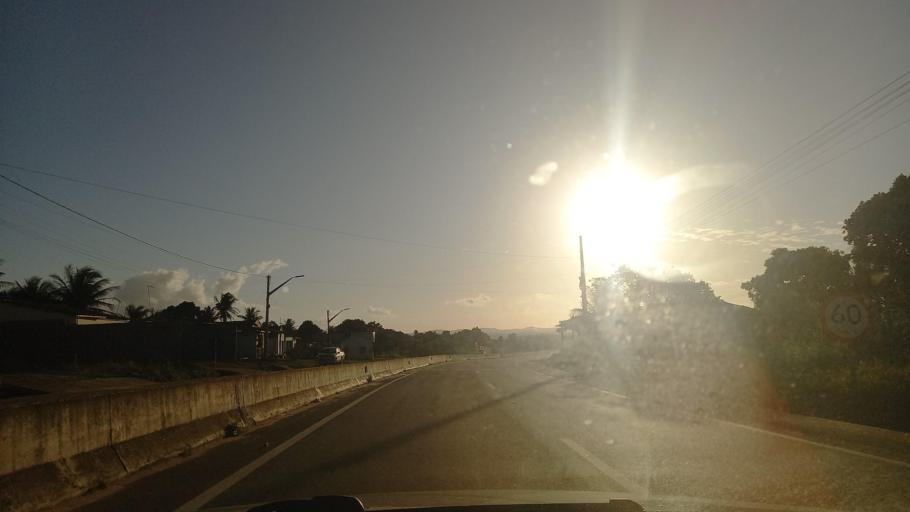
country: BR
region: Alagoas
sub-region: Limoeiro De Anadia
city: Limoeiro de Anadia
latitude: -9.7423
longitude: -36.4730
